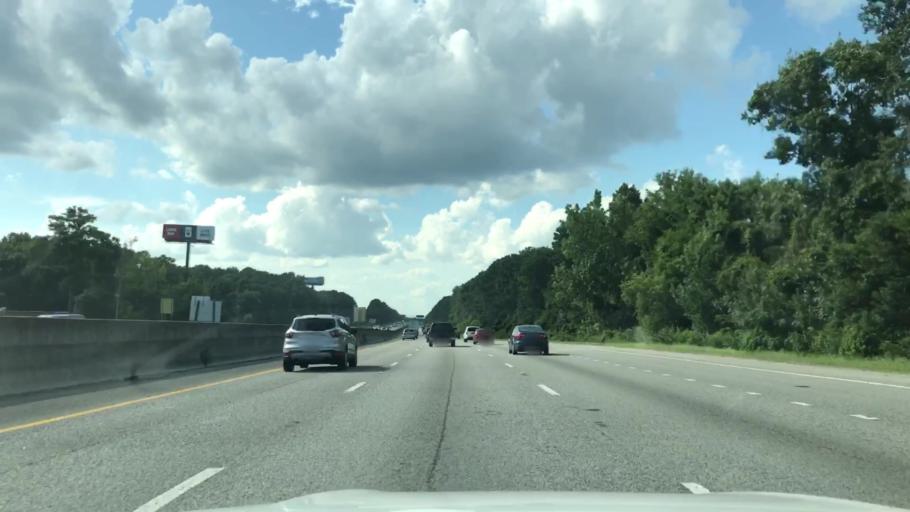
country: US
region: South Carolina
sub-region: Berkeley County
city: Hanahan
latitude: 32.9445
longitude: -80.0538
